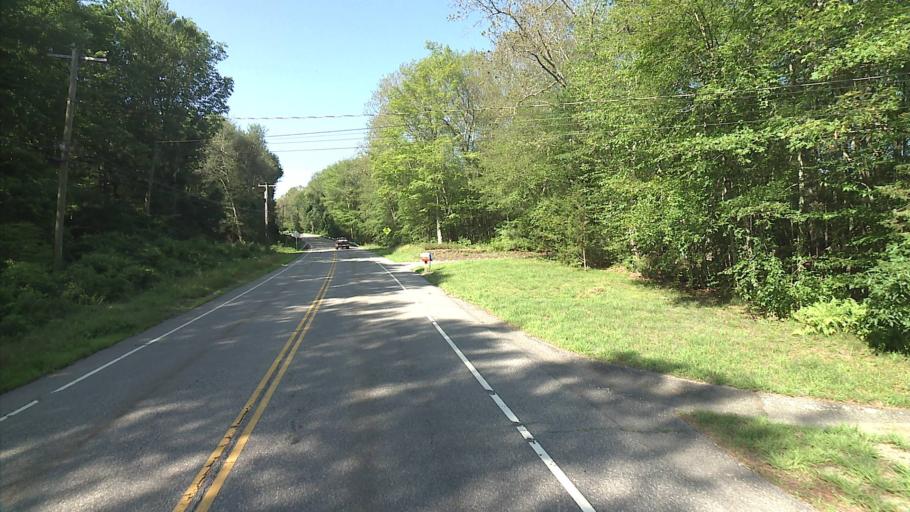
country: US
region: Connecticut
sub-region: New London County
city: Montville Center
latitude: 41.5336
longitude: -72.2036
